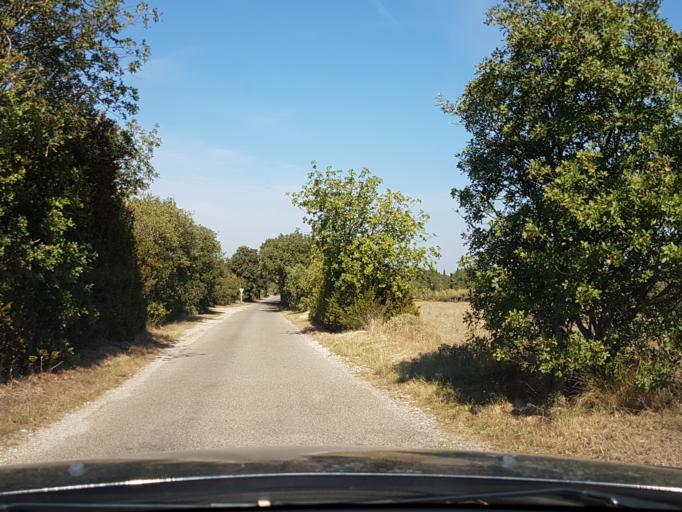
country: FR
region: Provence-Alpes-Cote d'Azur
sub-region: Departement des Bouches-du-Rhone
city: Eygalieres
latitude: 43.7689
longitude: 4.9563
